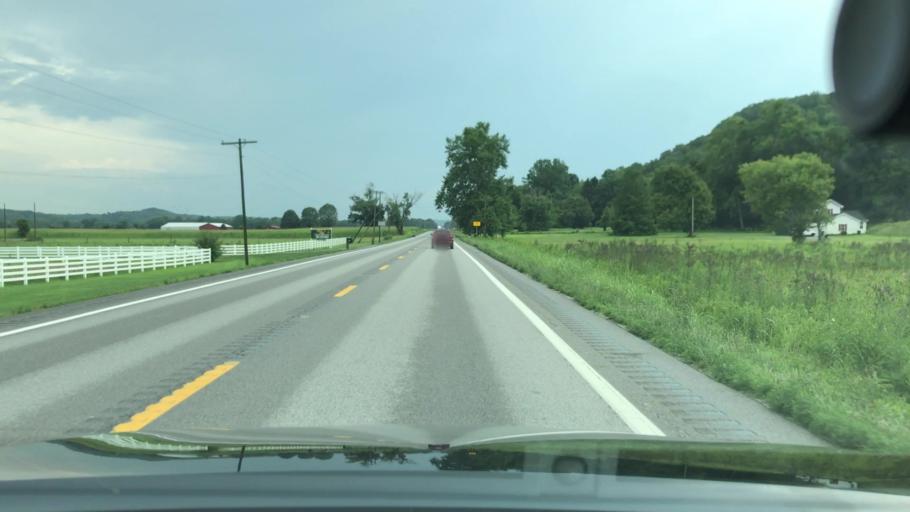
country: US
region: West Virginia
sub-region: Putnam County
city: Buffalo
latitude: 38.7064
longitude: -81.9670
